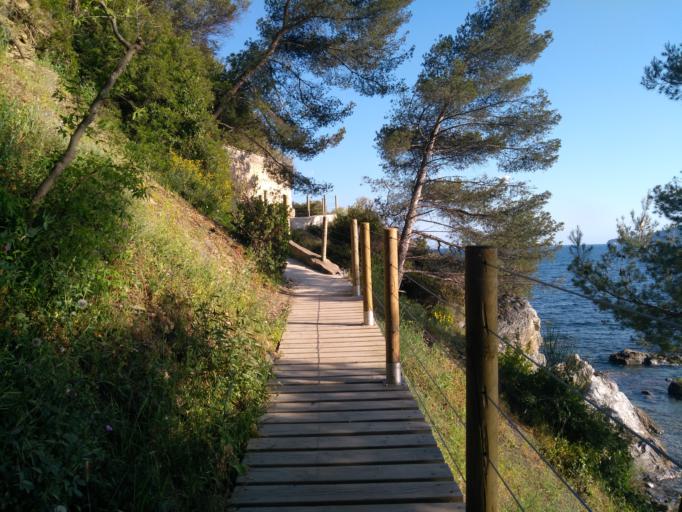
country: FR
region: Provence-Alpes-Cote d'Azur
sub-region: Departement du Var
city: Toulon
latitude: 43.1079
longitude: 5.9579
